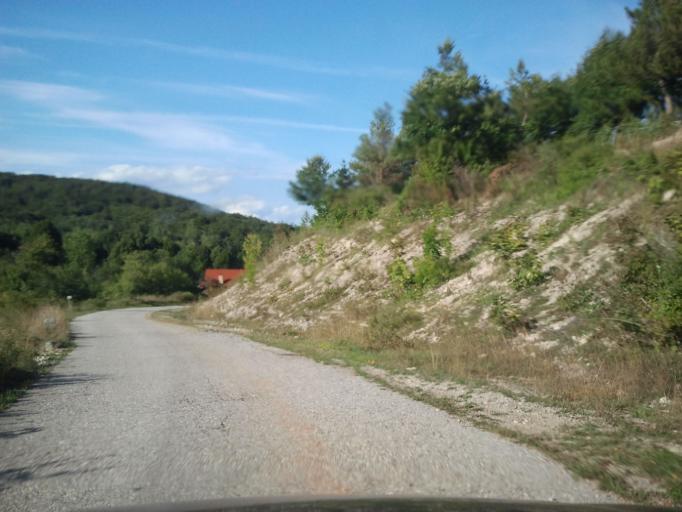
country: HR
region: Zadarska
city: Obrovac
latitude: 44.3321
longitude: 15.6397
